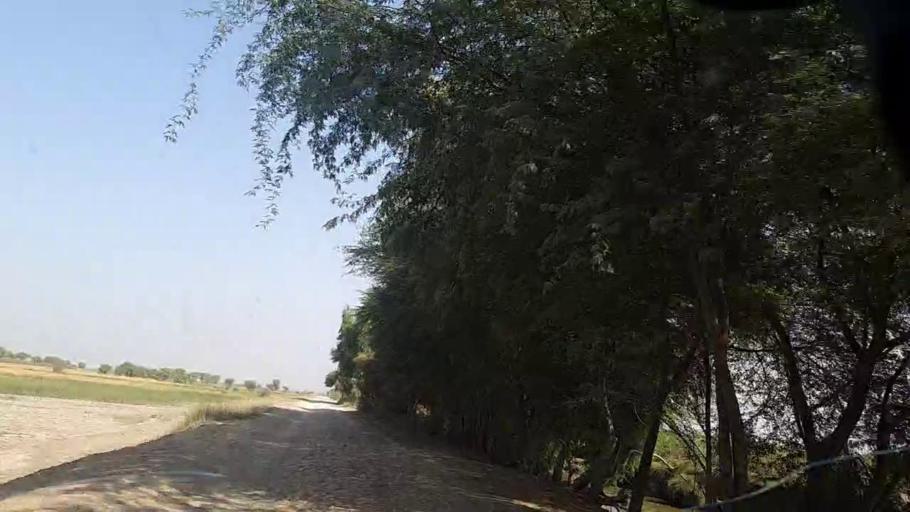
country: PK
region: Sindh
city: Rustam jo Goth
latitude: 28.0799
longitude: 68.8197
